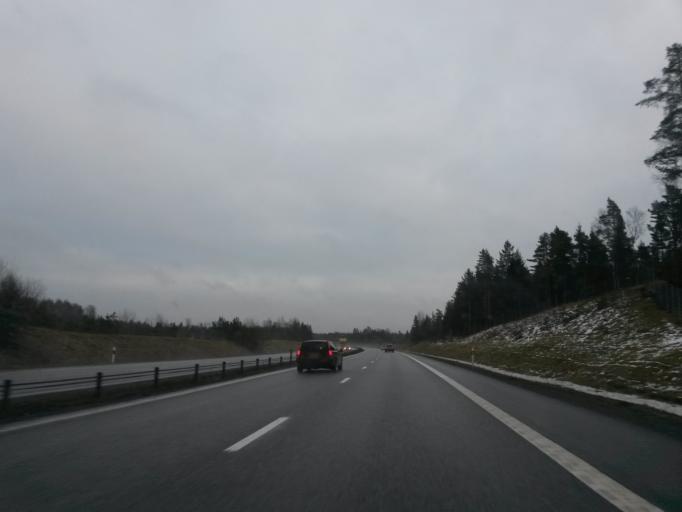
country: SE
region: Vaestra Goetaland
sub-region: Trollhattan
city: Sjuntorp
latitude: 58.3273
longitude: 12.1443
